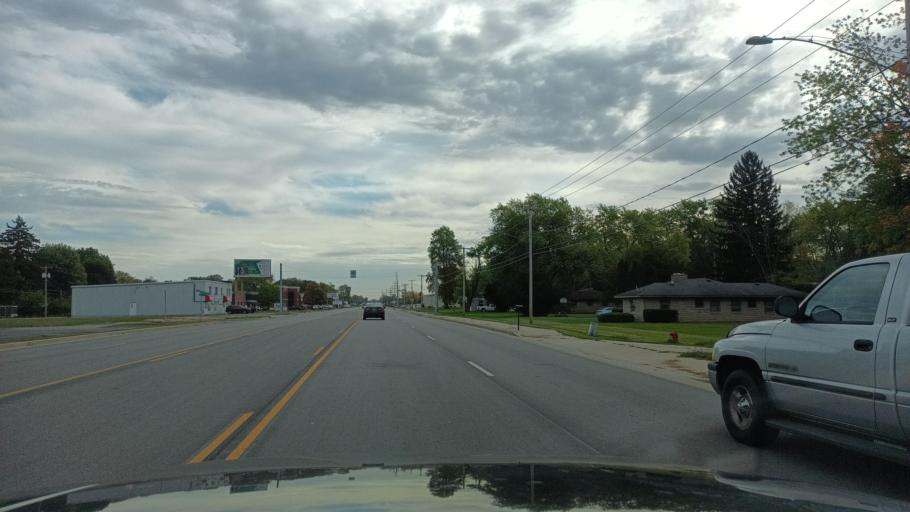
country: US
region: Indiana
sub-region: Delaware County
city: Yorktown
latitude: 40.1811
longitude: -85.4587
